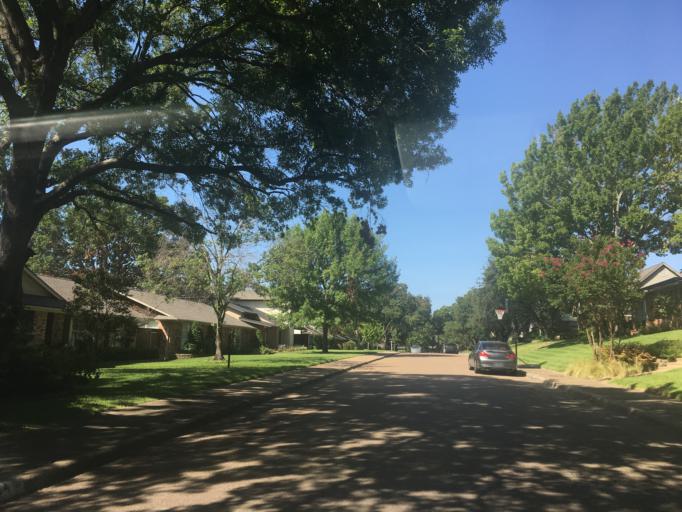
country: US
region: Texas
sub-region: Dallas County
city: Richardson
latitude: 32.8751
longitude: -96.7270
